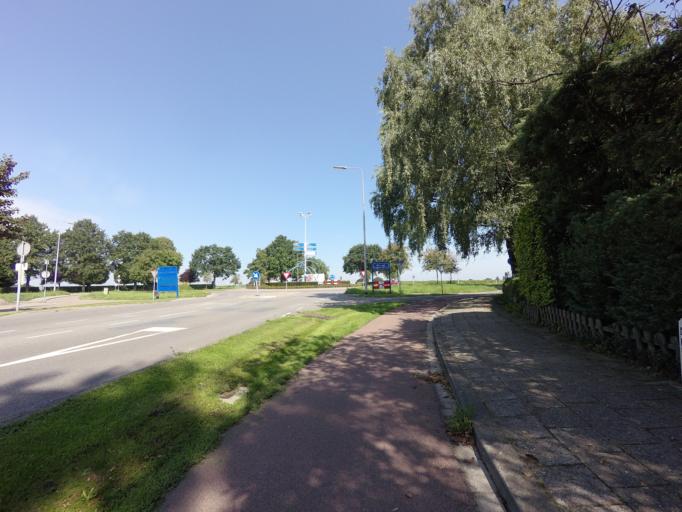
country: NL
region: Gelderland
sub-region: Berkelland
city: Neede
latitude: 52.1395
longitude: 6.6106
